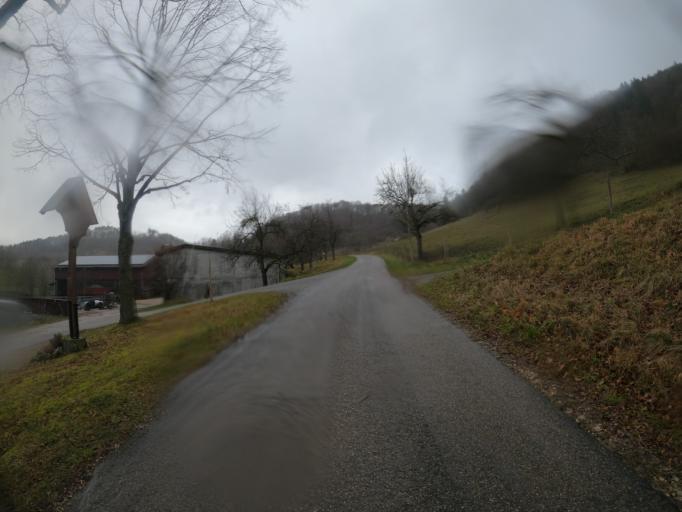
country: DE
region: Baden-Wuerttemberg
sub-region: Regierungsbezirk Stuttgart
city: Waldstetten
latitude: 48.7269
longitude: 9.8416
